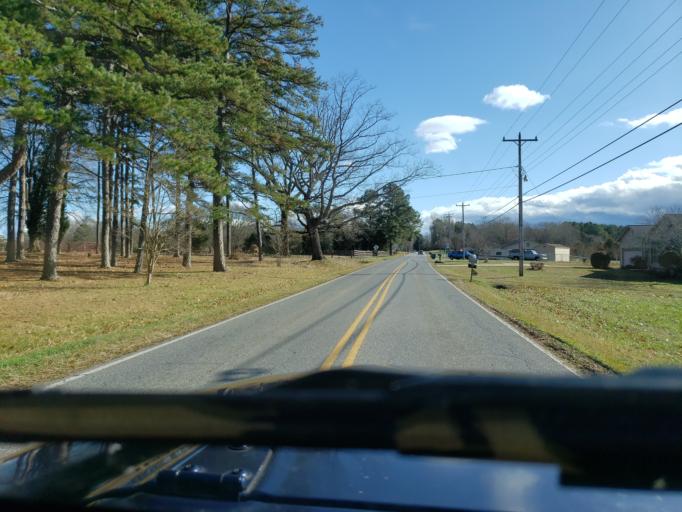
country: US
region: North Carolina
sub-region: Cleveland County
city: White Plains
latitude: 35.1823
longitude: -81.4610
